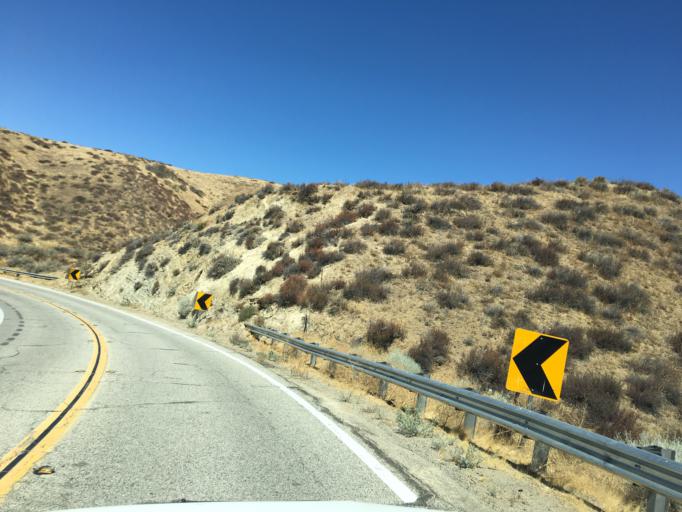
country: US
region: California
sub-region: Los Angeles County
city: Leona Valley
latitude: 34.6107
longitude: -118.2476
